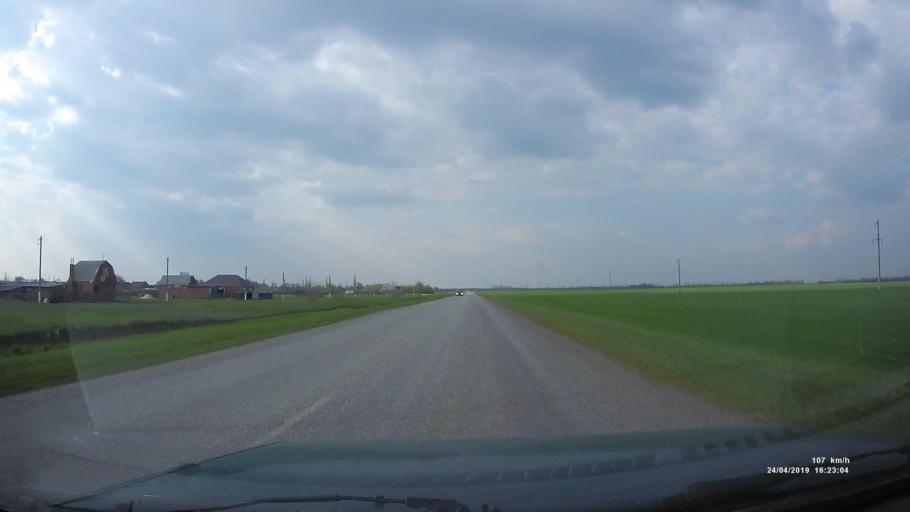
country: RU
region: Rostov
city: Orlovskiy
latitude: 46.8291
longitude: 42.0516
